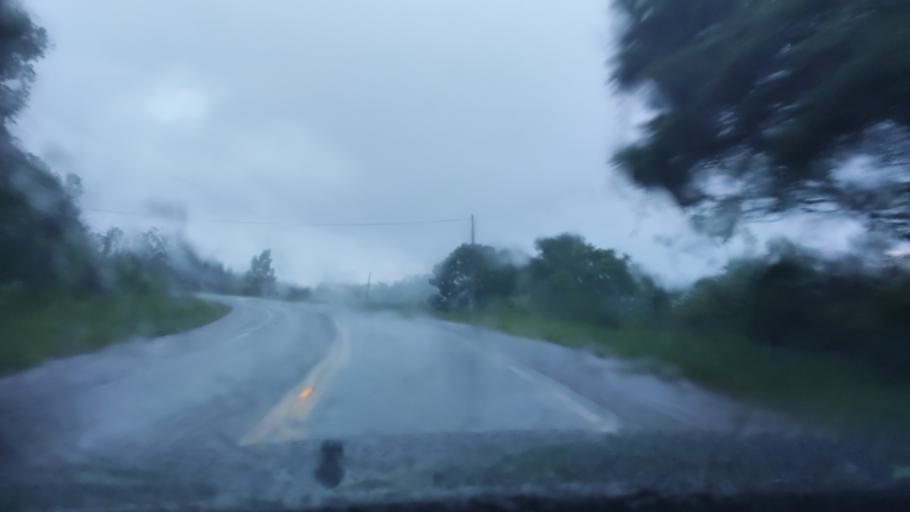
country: BR
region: Sao Paulo
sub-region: Socorro
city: Socorro
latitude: -22.7684
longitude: -46.5577
